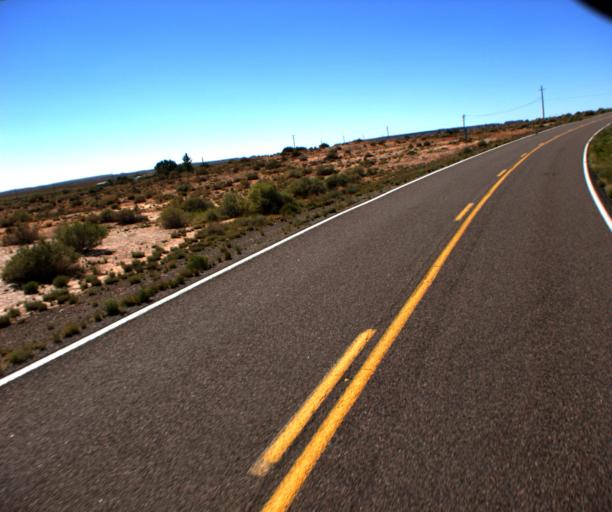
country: US
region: Arizona
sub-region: Coconino County
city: LeChee
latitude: 35.1261
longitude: -110.8744
